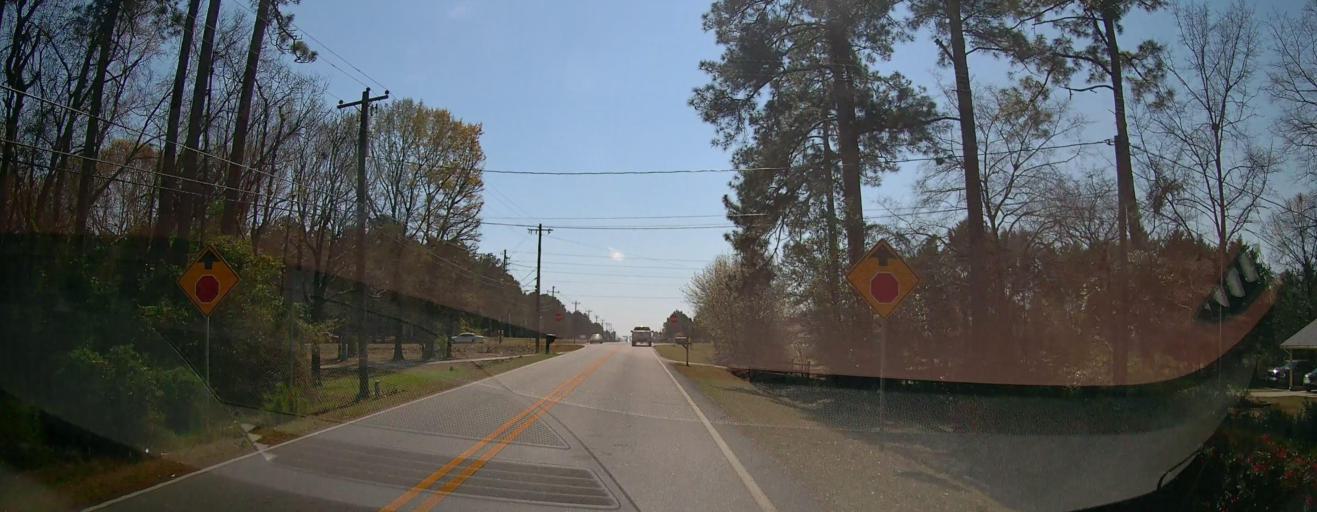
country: US
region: Georgia
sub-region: Houston County
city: Centerville
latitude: 32.5868
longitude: -83.6945
